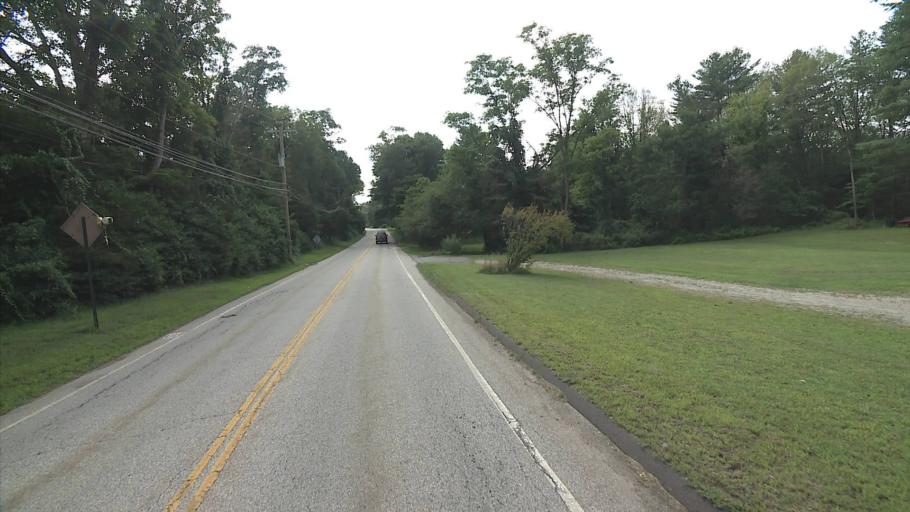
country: US
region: Connecticut
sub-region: Middlesex County
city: East Haddam
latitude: 41.4417
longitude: -72.4178
